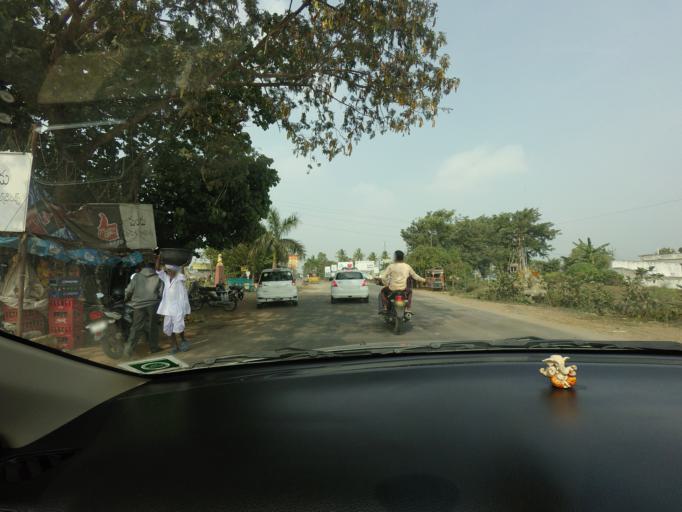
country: IN
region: Andhra Pradesh
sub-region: Krishna
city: Kankipadu
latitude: 16.4519
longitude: 80.7713
